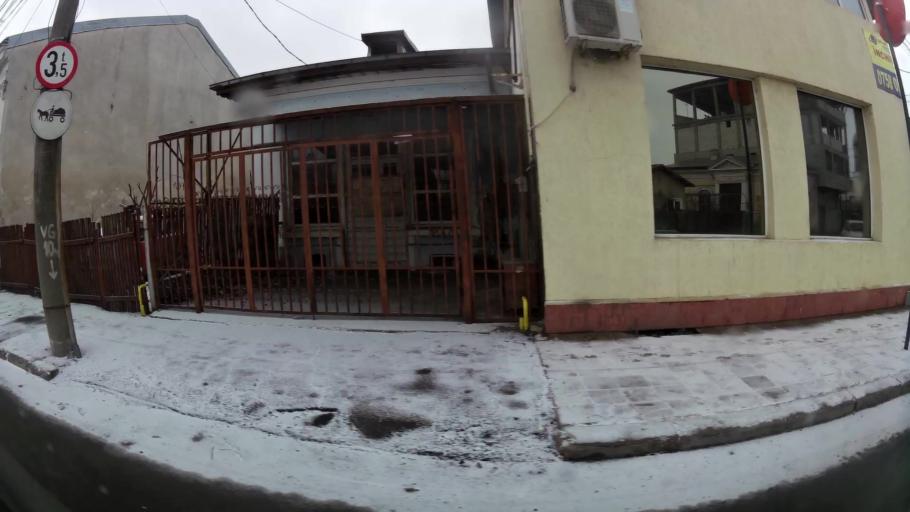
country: RO
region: Prahova
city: Ploiesti
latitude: 44.9495
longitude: 26.0193
